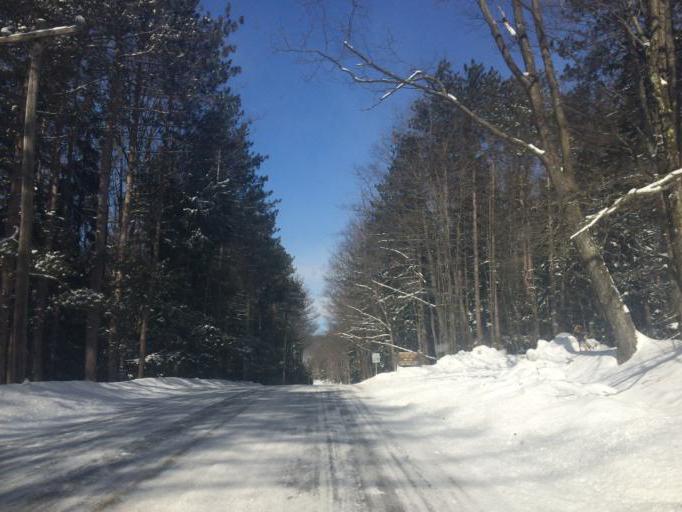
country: US
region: Pennsylvania
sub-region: Centre County
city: Stormstown
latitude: 40.9079
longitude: -78.0544
